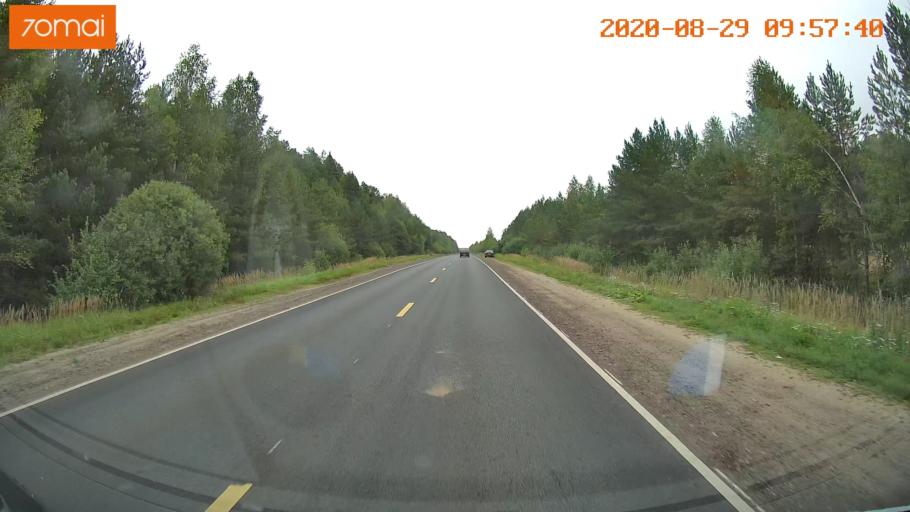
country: RU
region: Ivanovo
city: Zarechnyy
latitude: 57.4157
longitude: 42.3199
